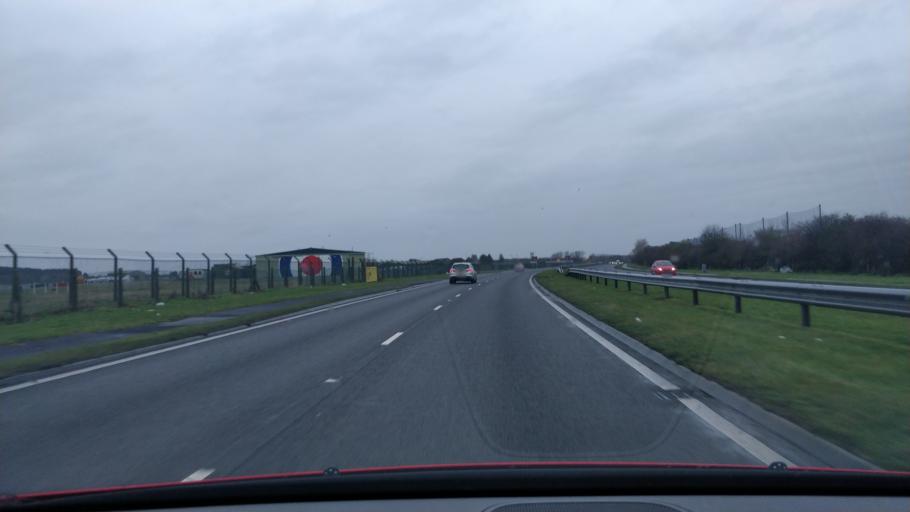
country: GB
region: England
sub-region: Sefton
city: Formby
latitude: 53.5792
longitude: -3.0503
